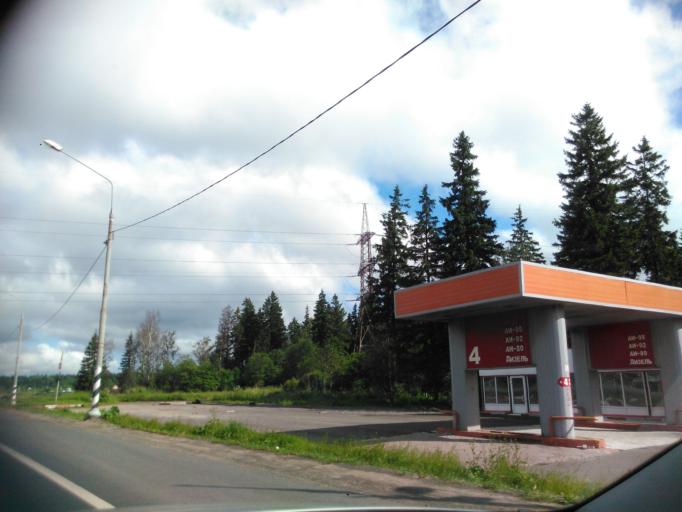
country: RU
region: Moskovskaya
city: Solnechnogorsk
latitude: 56.2375
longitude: 36.8973
